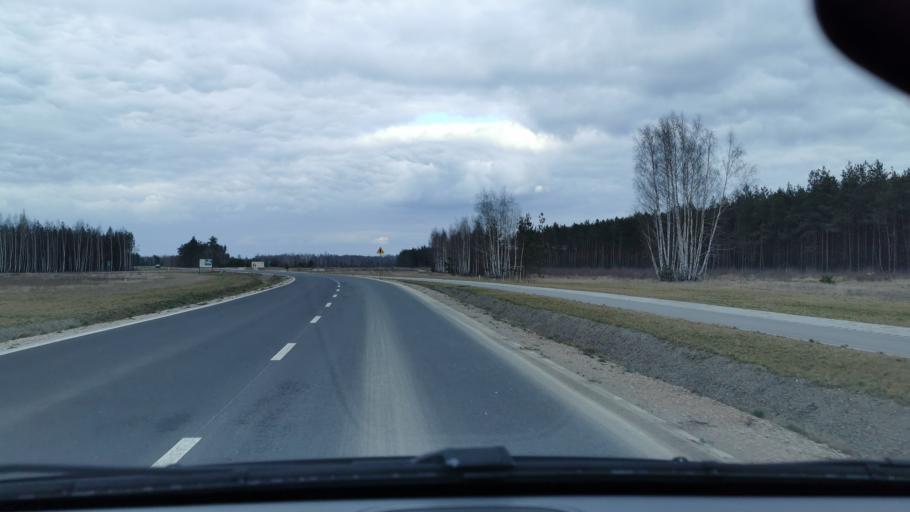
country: PL
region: Masovian Voivodeship
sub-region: Powiat zyrardowski
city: Zyrardow
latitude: 51.9934
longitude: 20.4647
